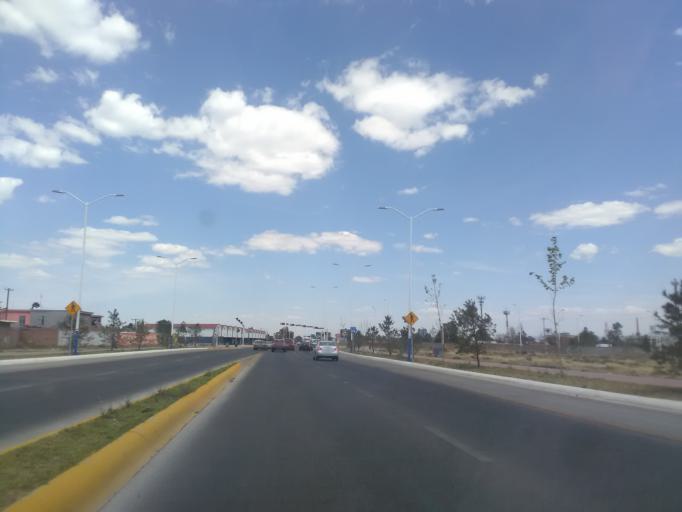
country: MX
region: Durango
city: Victoria de Durango
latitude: 24.0372
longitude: -104.6618
